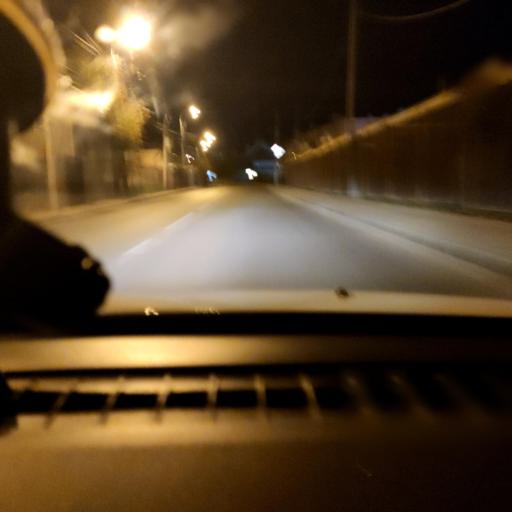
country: RU
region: Samara
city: Samara
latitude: 53.2691
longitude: 50.1975
